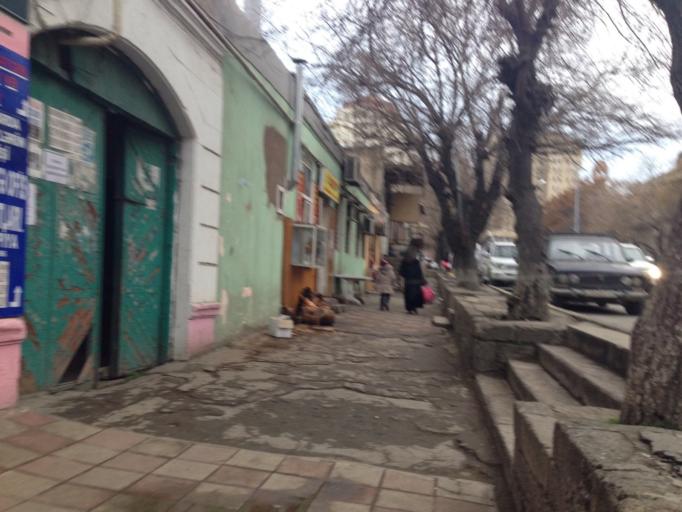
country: AZ
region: Baki
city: Baku
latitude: 40.3873
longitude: 49.8522
